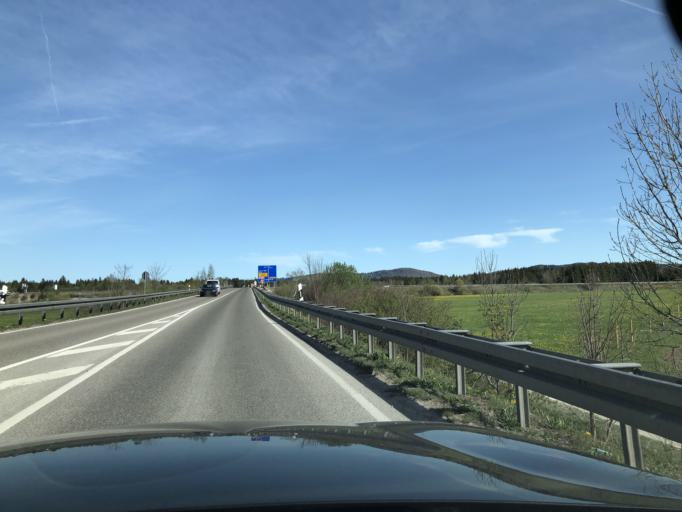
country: DE
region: Bavaria
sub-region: Swabia
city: Fuessen
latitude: 47.5712
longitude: 10.6650
